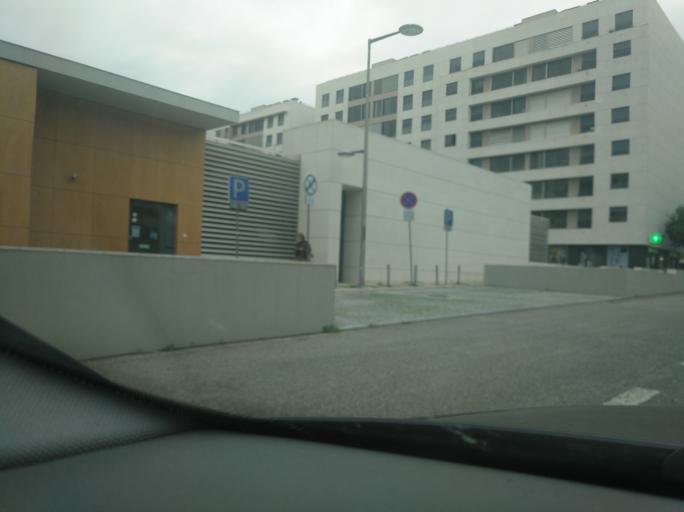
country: PT
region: Lisbon
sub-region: Odivelas
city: Pontinha
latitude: 38.7478
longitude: -9.1781
